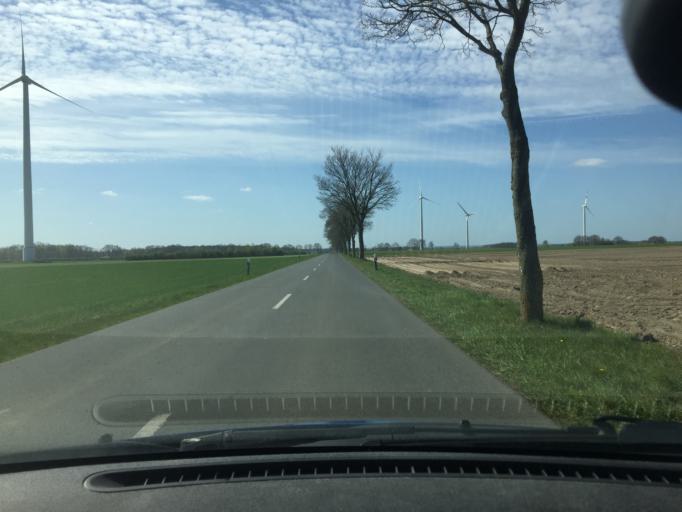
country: DE
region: Lower Saxony
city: Ratzlingen
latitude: 52.9502
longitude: 10.6649
